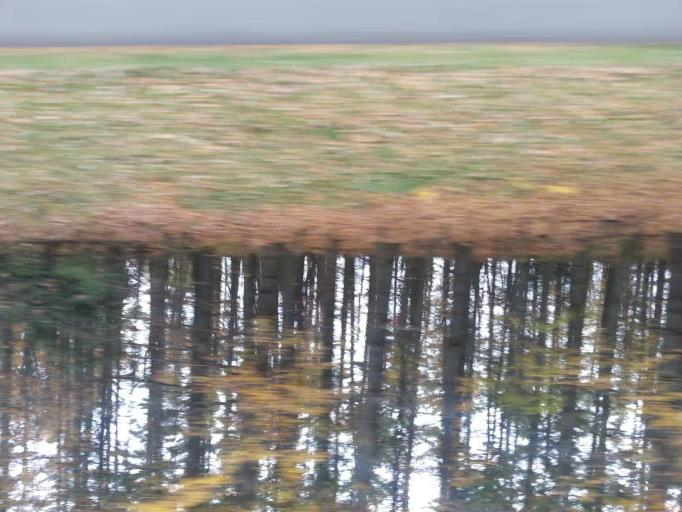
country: US
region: North Carolina
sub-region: Ashe County
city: Jefferson
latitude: 36.3461
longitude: -81.3749
